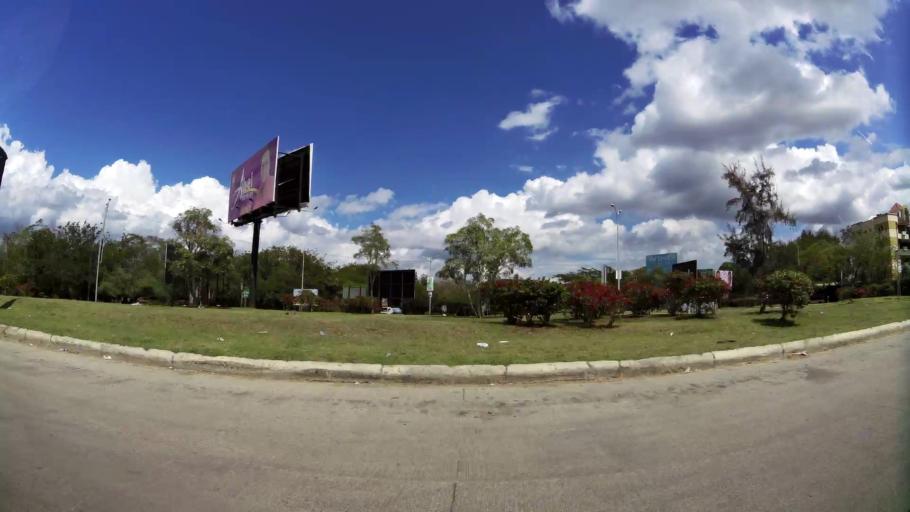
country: DO
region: Santiago
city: Santiago de los Caballeros
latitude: 19.4252
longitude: -70.6833
